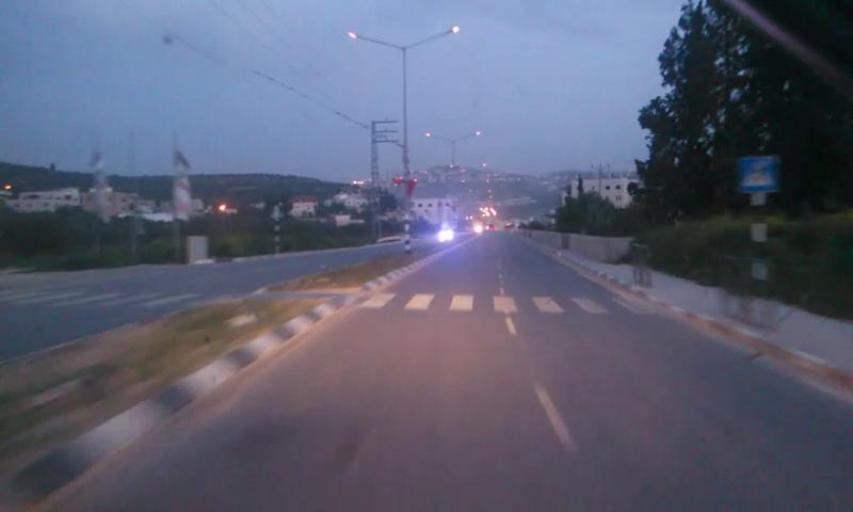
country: PS
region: West Bank
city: Dayr Sharaf
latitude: 32.2499
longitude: 35.1898
